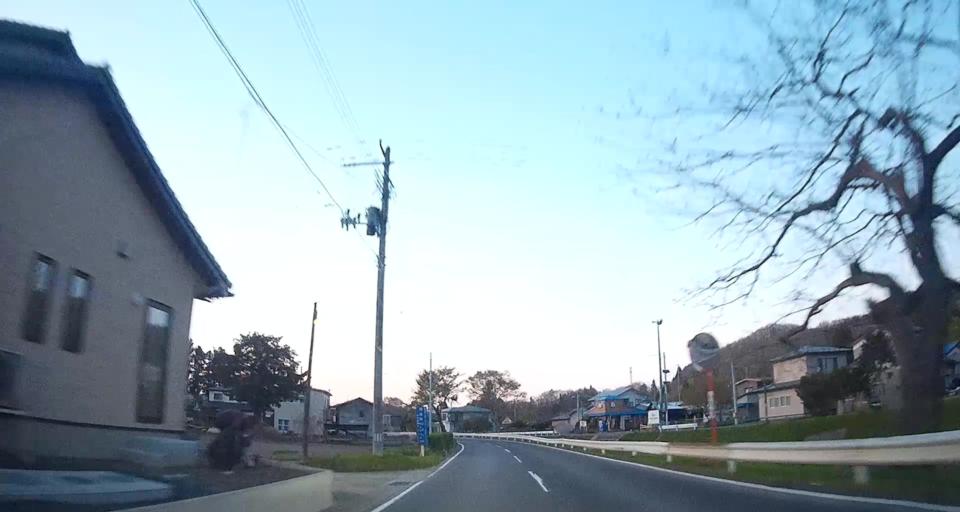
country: JP
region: Aomori
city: Hachinohe
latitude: 40.1772
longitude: 141.7759
